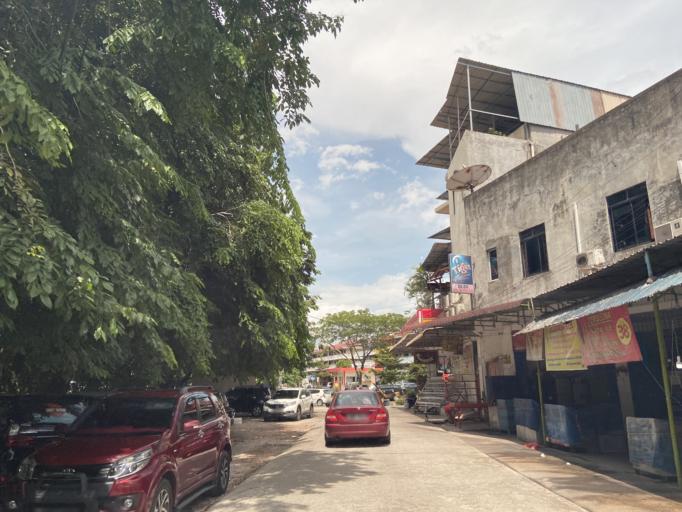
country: SG
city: Singapore
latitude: 1.1421
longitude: 104.0113
